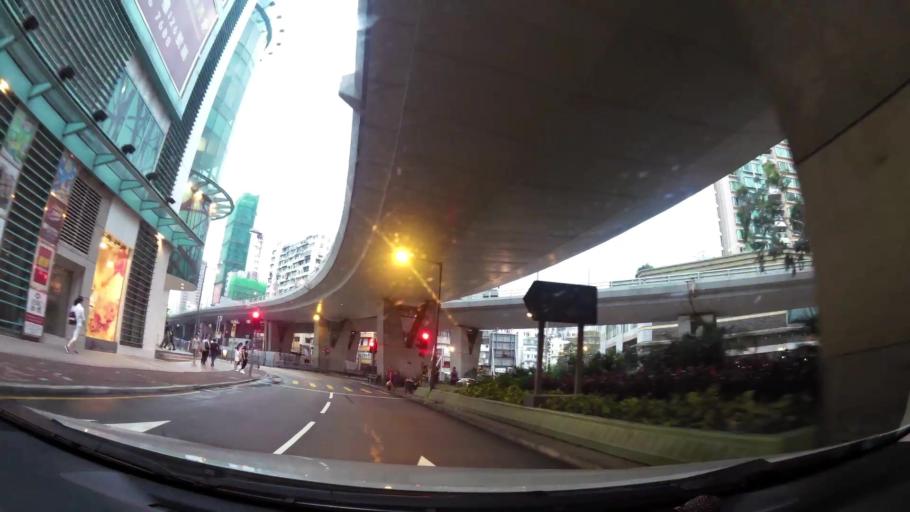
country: HK
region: Sham Shui Po
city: Sham Shui Po
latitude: 22.3246
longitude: 114.1618
